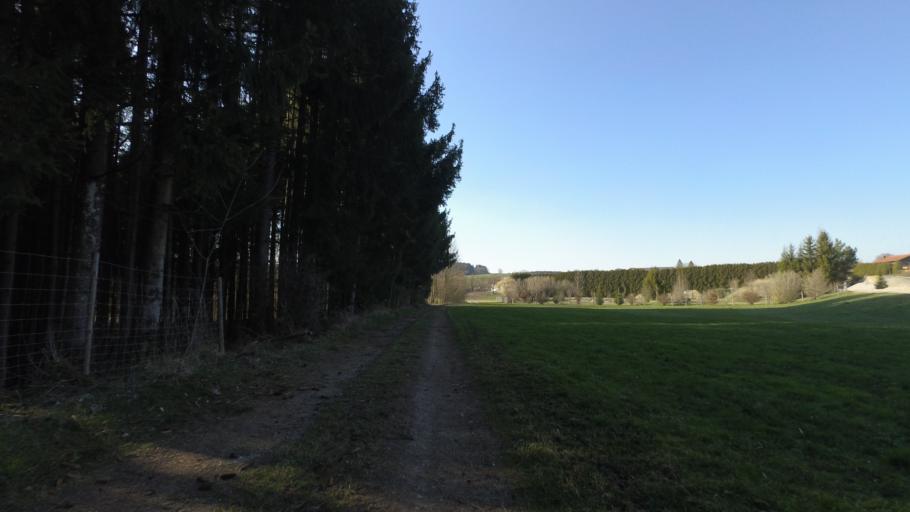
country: DE
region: Bavaria
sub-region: Upper Bavaria
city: Chieming
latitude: 47.9402
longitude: 12.5474
